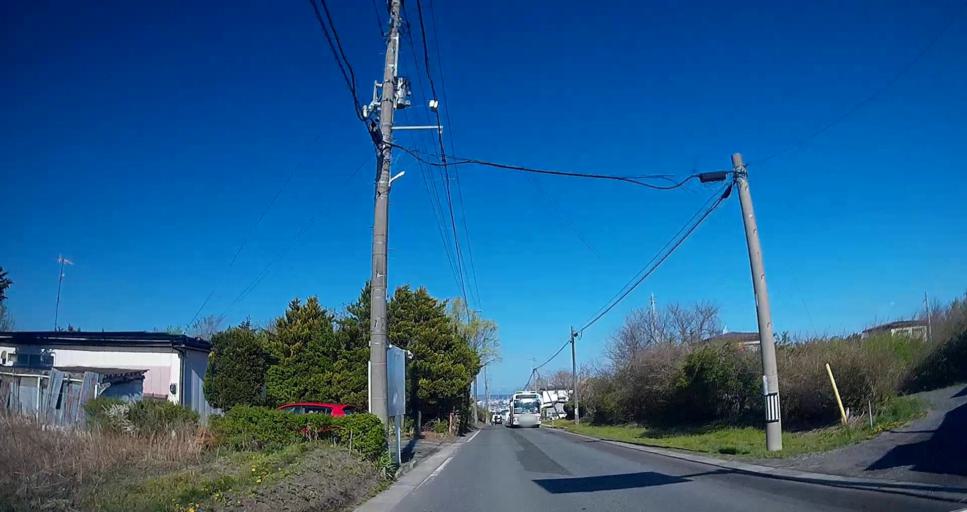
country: JP
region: Aomori
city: Hachinohe
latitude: 40.5221
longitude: 141.5638
